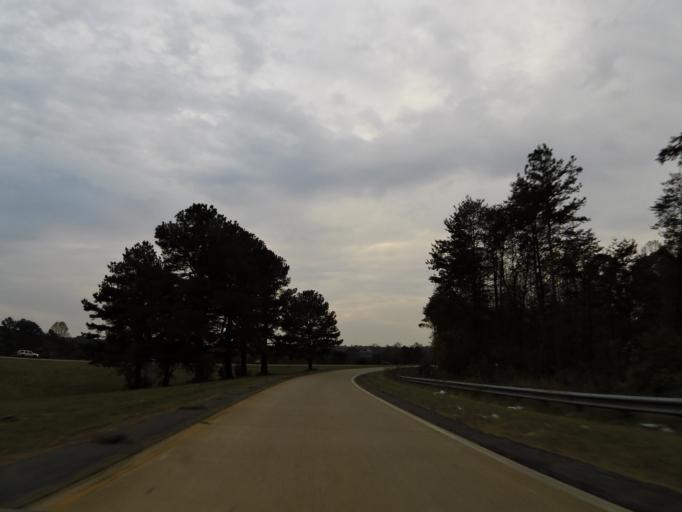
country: US
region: North Carolina
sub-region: Catawba County
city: Hickory
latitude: 35.7093
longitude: -81.3563
